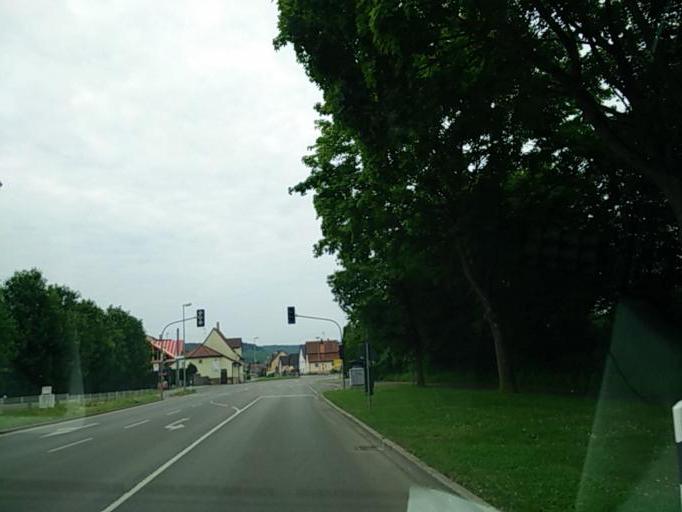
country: DE
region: Baden-Wuerttemberg
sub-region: Tuebingen Region
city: Tuebingen
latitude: 48.4964
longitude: 9.0315
